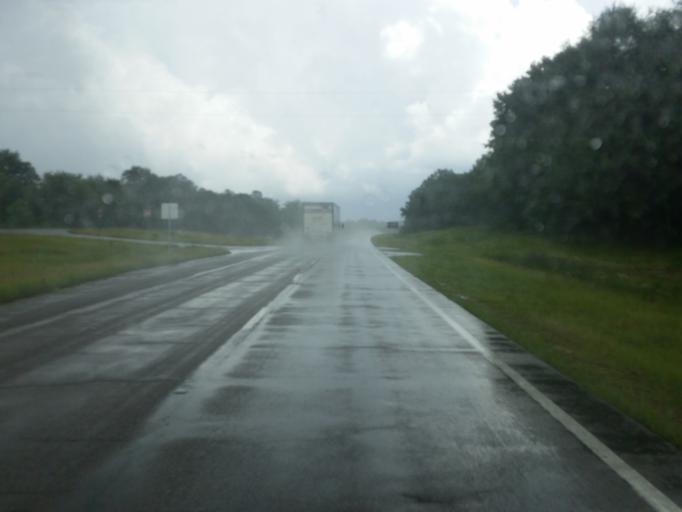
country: US
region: Mississippi
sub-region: George County
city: Lucedale
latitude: 30.9004
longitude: -88.4610
